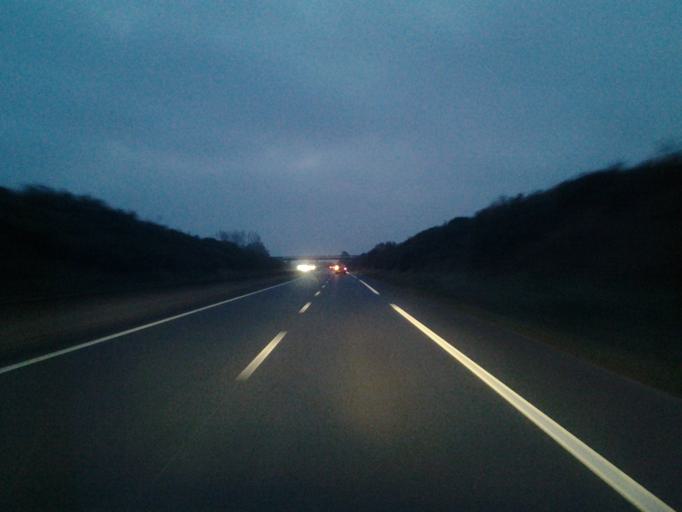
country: FR
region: Pays de la Loire
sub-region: Departement de la Vendee
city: Les Clouzeaux
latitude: 46.6394
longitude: -1.4991
